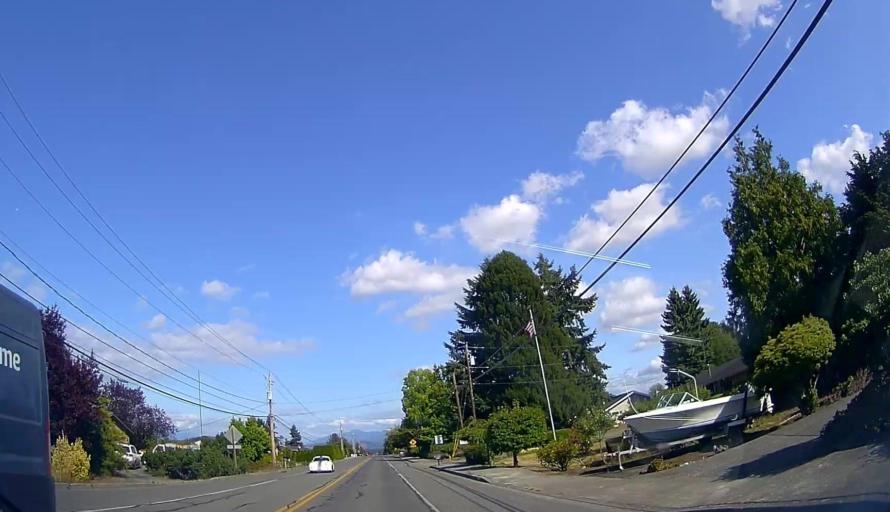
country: US
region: Washington
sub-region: Skagit County
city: Burlington
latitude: 48.4721
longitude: -122.3847
